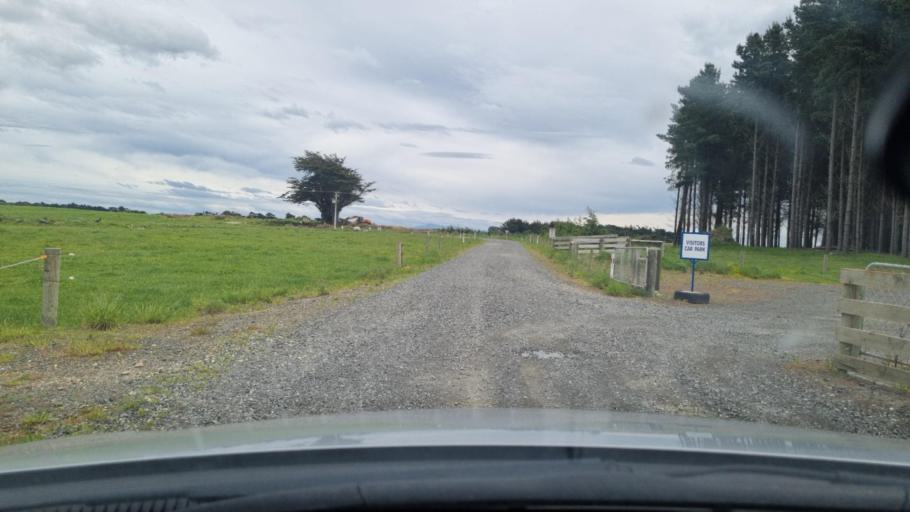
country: NZ
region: Southland
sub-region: Invercargill City
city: Invercargill
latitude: -46.4078
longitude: 168.2741
